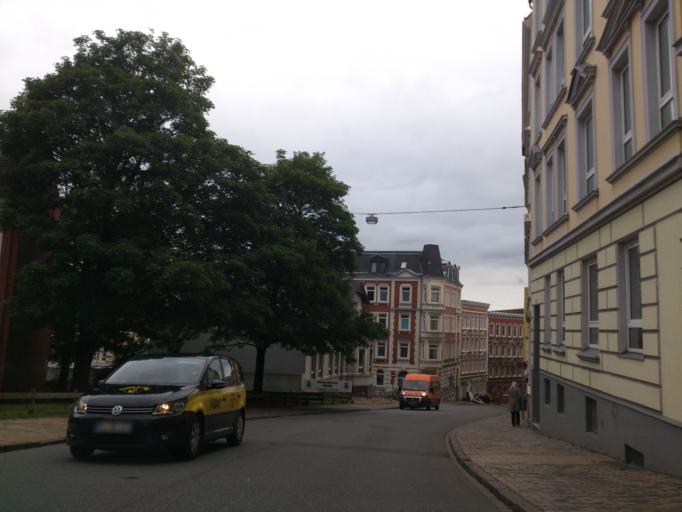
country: DE
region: Schleswig-Holstein
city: Flensburg
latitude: 54.7943
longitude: 9.4260
